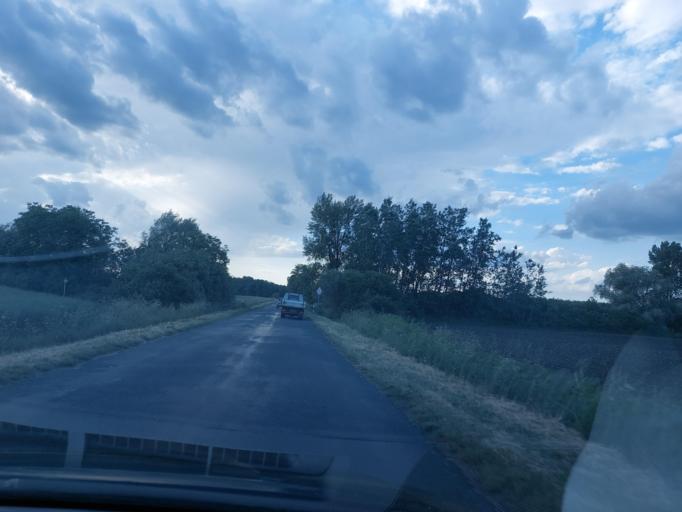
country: HU
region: Veszprem
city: Devecser
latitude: 47.1865
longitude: 17.3566
